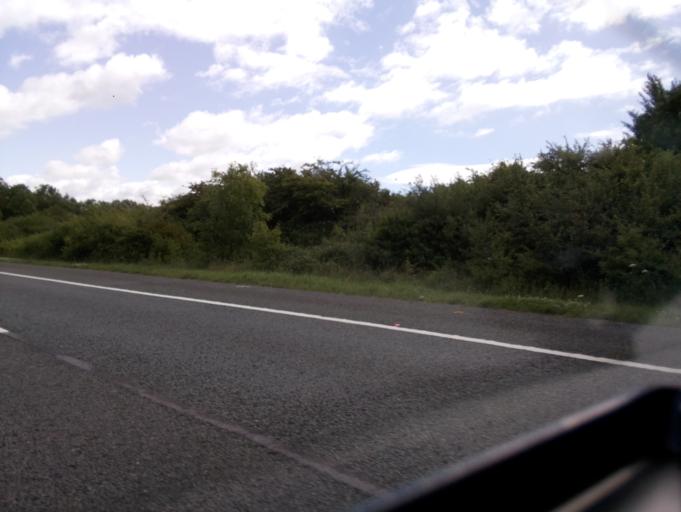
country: GB
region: England
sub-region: South Gloucestershire
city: Severn Beach
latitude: 51.5700
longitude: -2.6352
